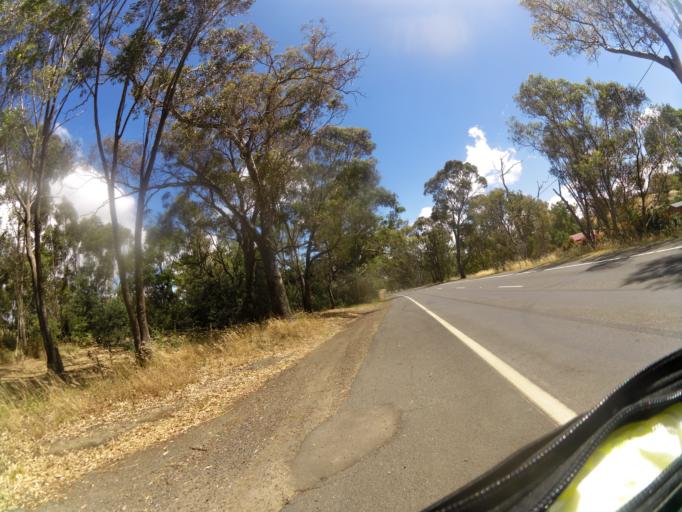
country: AU
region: Victoria
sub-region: Mount Alexander
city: Castlemaine
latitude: -37.0014
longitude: 144.2539
